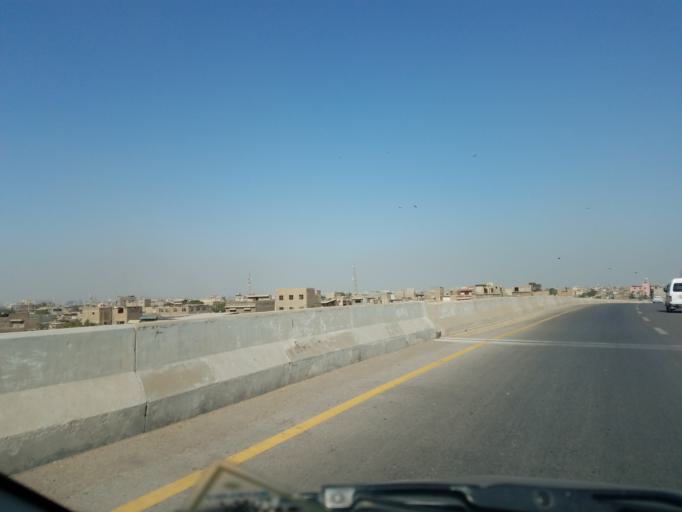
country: PK
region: Sindh
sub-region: Karachi District
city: Karachi
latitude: 24.8816
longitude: 66.9942
